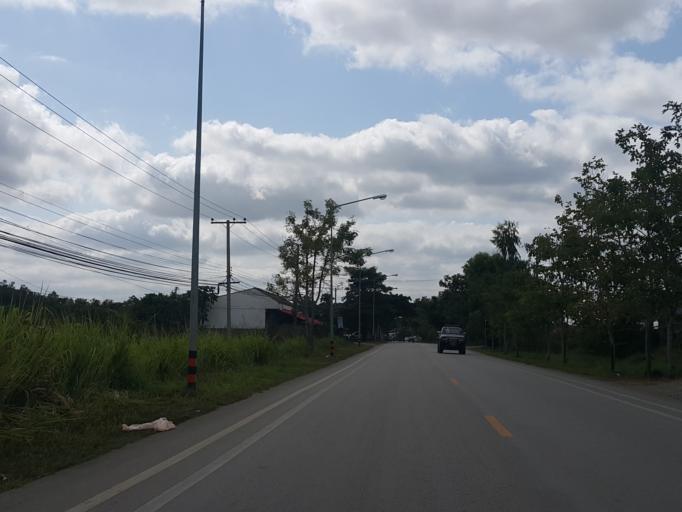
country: TH
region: Lamphun
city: Ban Thi
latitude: 18.6186
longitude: 99.0948
